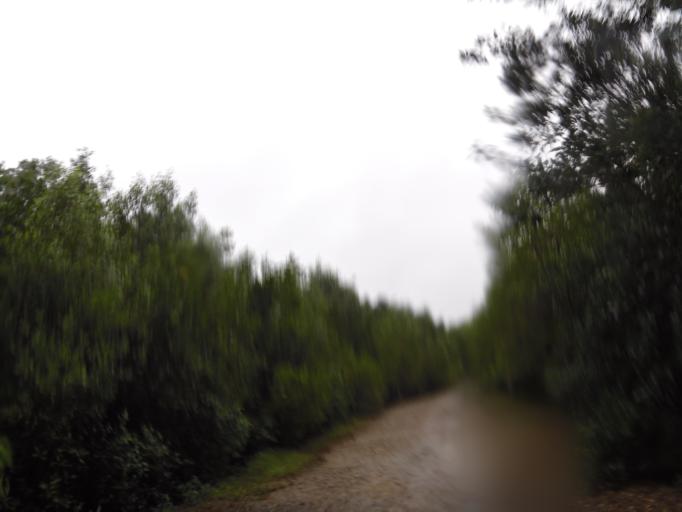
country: AU
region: Queensland
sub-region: Cairns
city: Cairns
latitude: -16.9000
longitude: 145.7543
